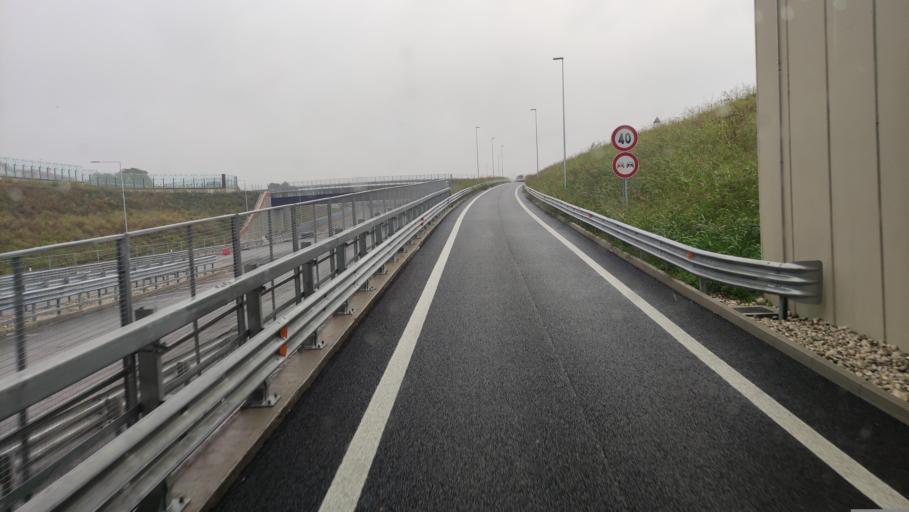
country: IT
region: Veneto
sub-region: Provincia di Treviso
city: Spresiano
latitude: 45.7504
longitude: 12.2589
